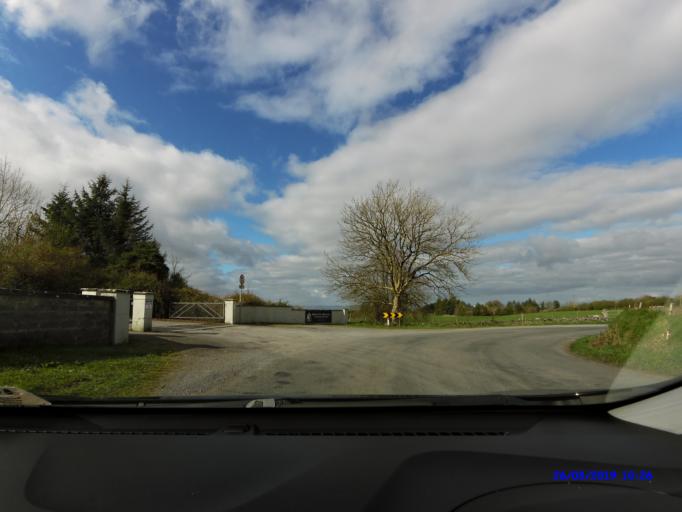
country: IE
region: Connaught
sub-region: Maigh Eo
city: Claremorris
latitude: 53.7331
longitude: -9.0019
